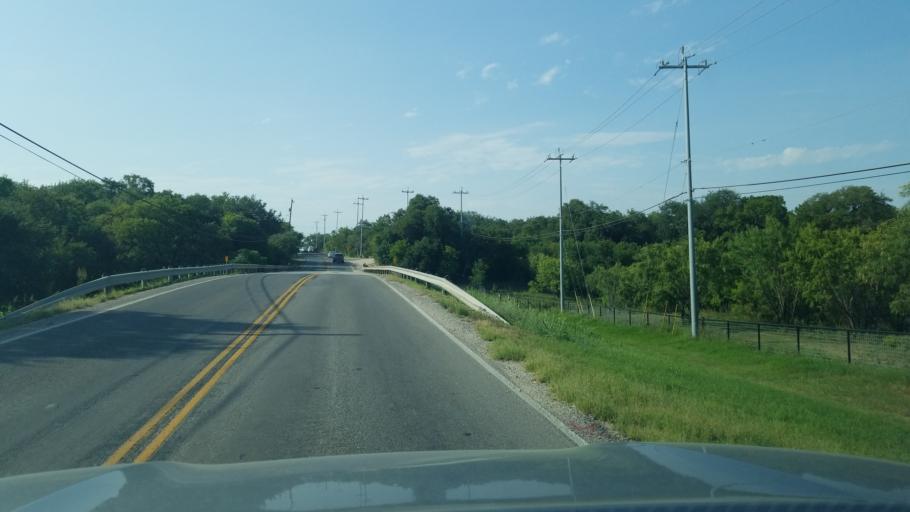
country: US
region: Texas
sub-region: Bexar County
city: Leon Valley
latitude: 29.4468
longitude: -98.7526
